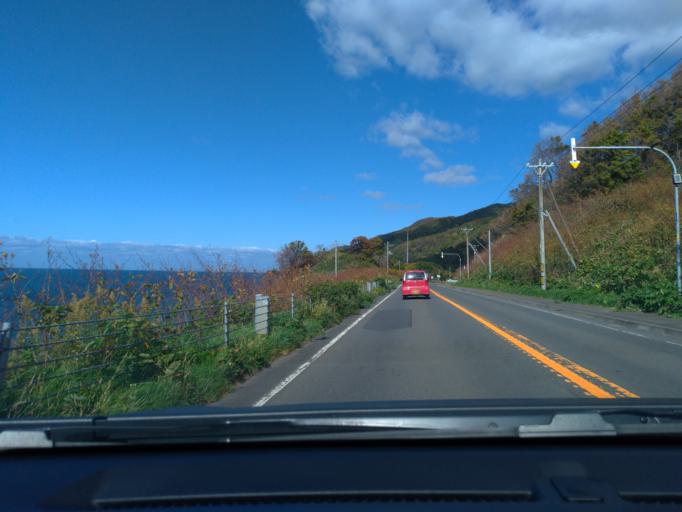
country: JP
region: Hokkaido
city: Ishikari
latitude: 43.4171
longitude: 141.4298
